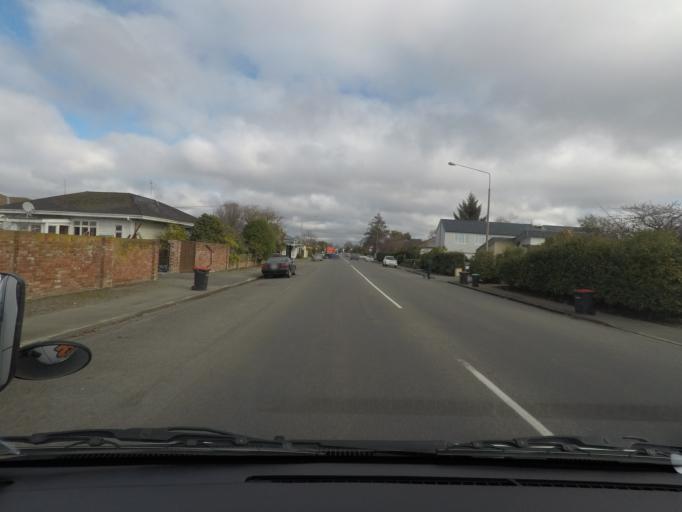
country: NZ
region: Canterbury
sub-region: Christchurch City
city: Christchurch
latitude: -43.5103
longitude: 172.6284
